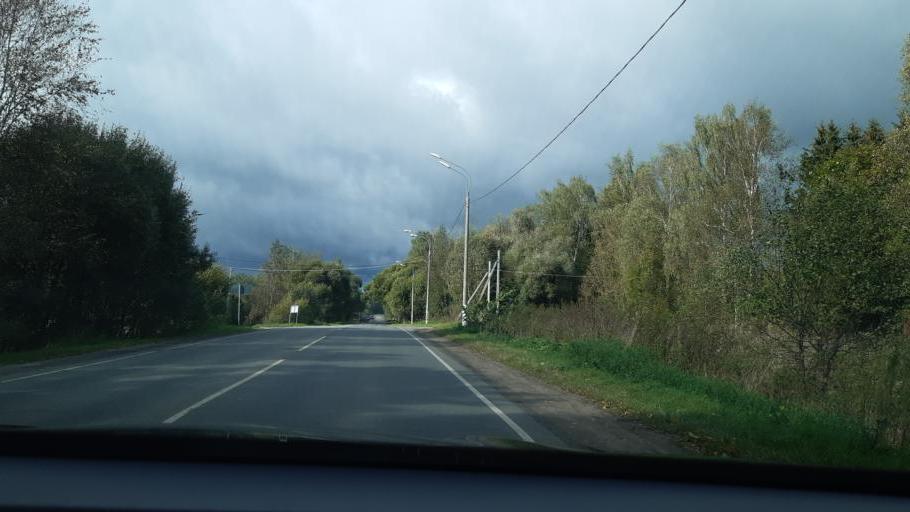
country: RU
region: Moskovskaya
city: Melikhovo
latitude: 55.1139
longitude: 37.6444
